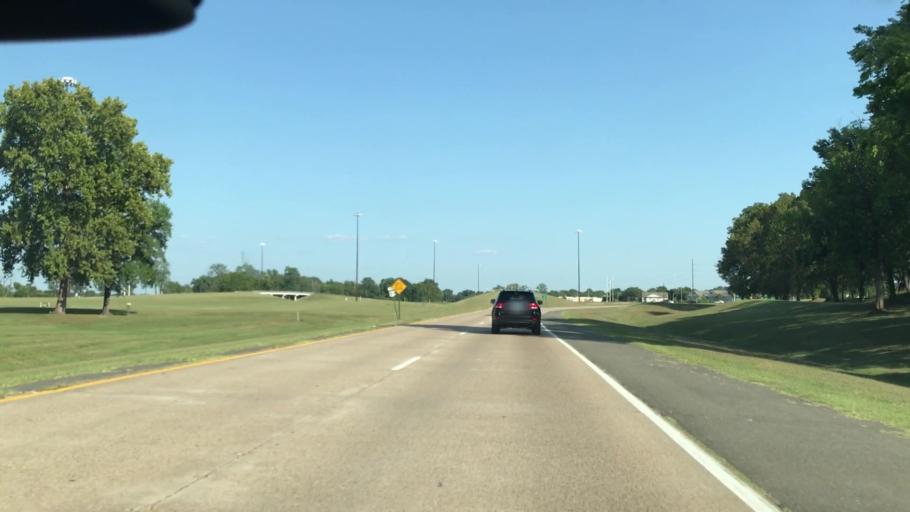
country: US
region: Louisiana
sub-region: Bossier Parish
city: Bossier City
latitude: 32.5045
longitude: -93.7195
